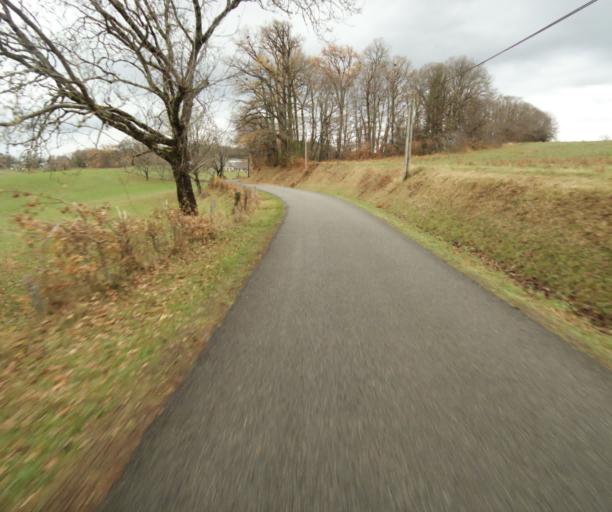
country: FR
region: Limousin
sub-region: Departement de la Correze
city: Saint-Mexant
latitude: 45.2817
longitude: 1.6327
